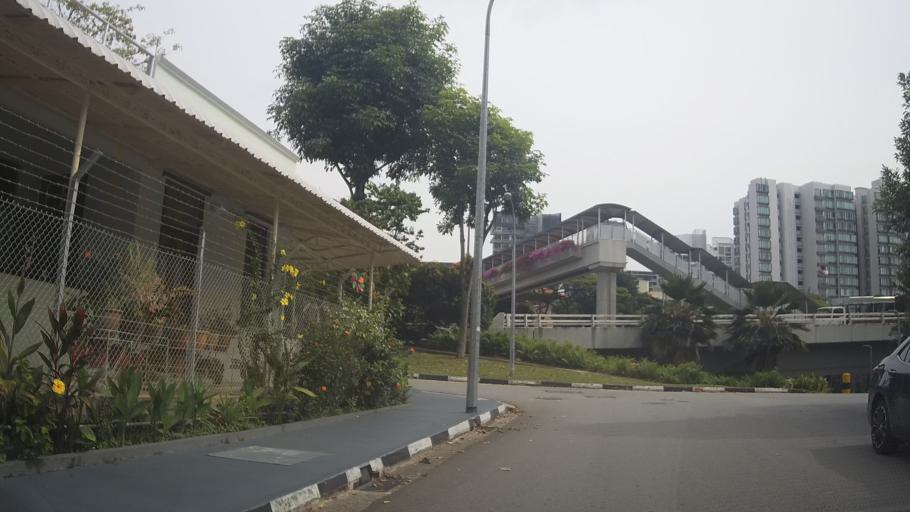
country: SG
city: Singapore
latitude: 1.3283
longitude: 103.8655
